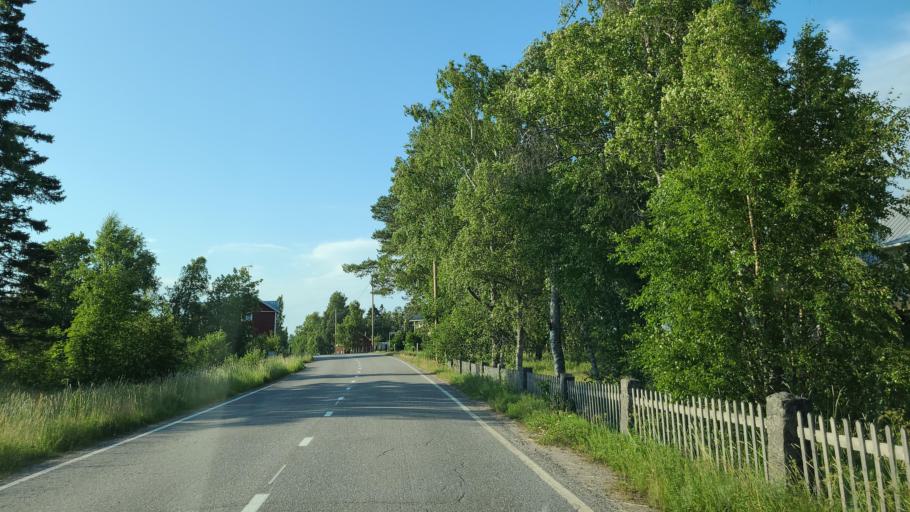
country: FI
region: Ostrobothnia
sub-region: Vaasa
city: Replot
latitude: 63.3383
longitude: 21.3315
